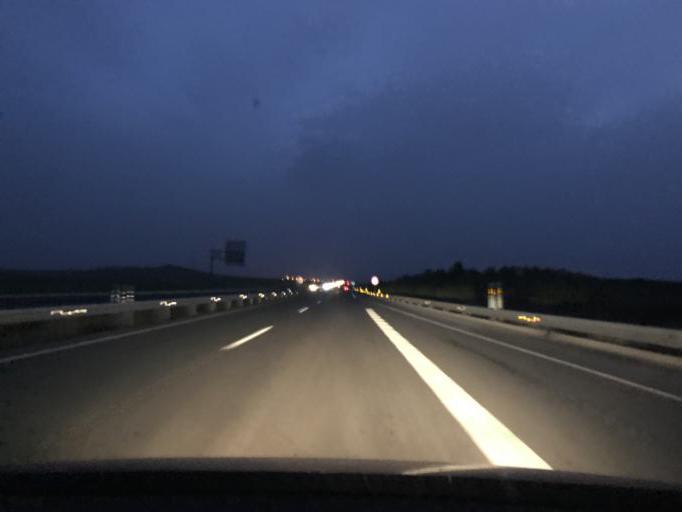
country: ES
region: Andalusia
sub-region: Provincia de Granada
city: Gor
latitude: 37.3880
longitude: -3.0467
